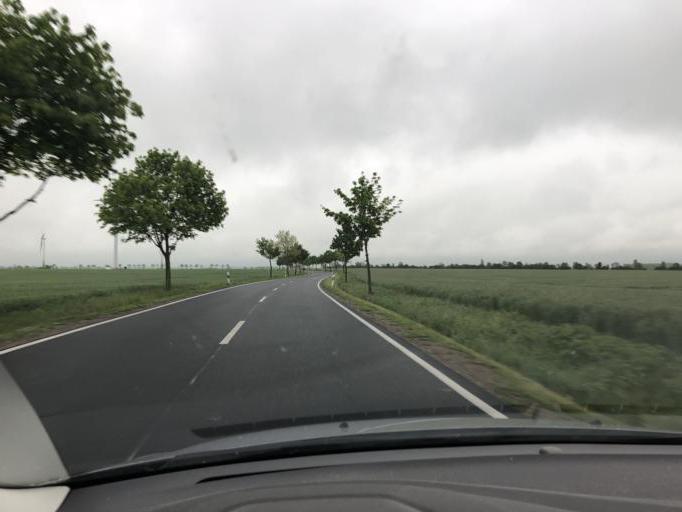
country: DE
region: Saxony
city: Dobernitz
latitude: 51.5080
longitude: 12.3766
